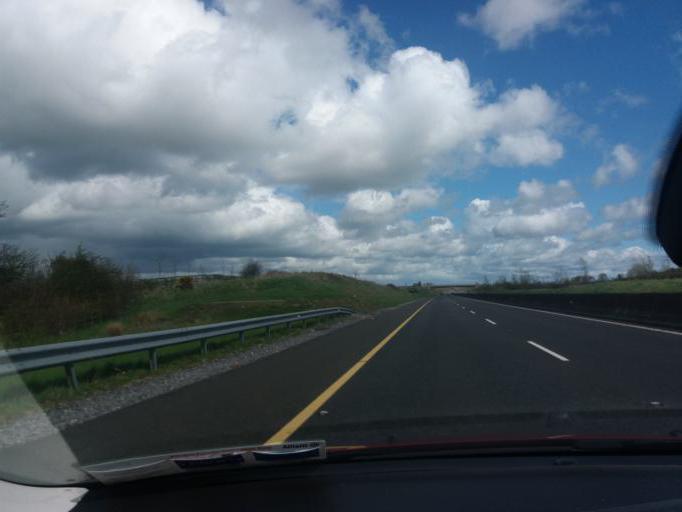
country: IE
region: Leinster
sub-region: Laois
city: Rathdowney
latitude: 52.7859
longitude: -7.5272
